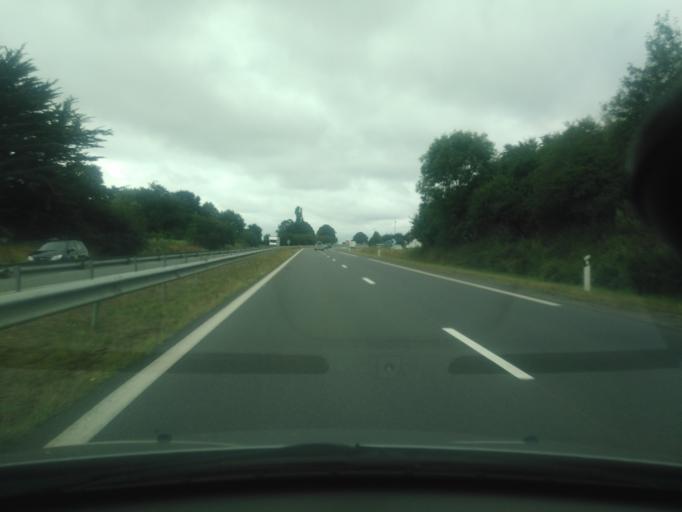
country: FR
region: Brittany
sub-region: Departement des Cotes-d'Armor
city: Quevert
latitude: 48.4484
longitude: -2.0938
